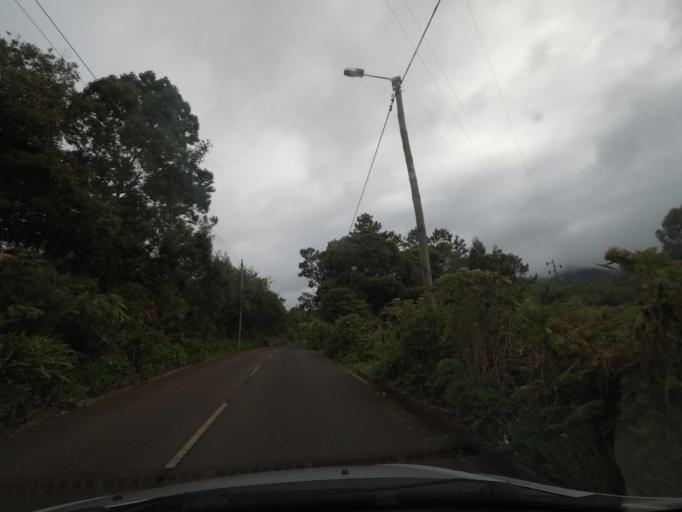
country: PT
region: Madeira
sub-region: Santana
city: Santana
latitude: 32.7864
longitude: -16.8765
